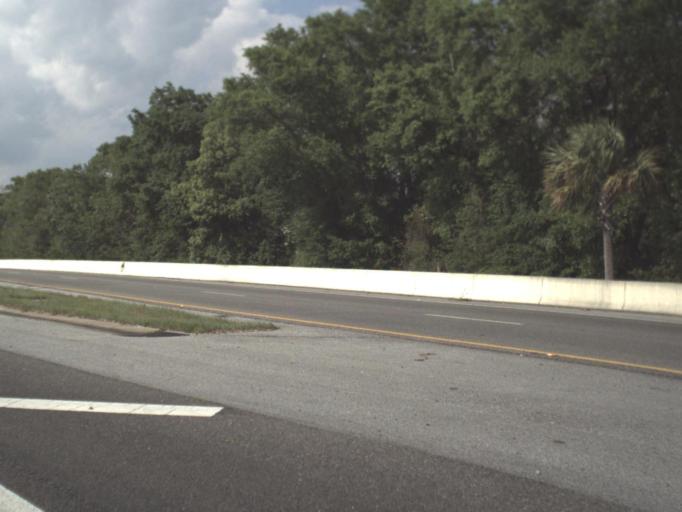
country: US
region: Florida
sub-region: Escambia County
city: Brent
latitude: 30.4690
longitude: -87.2273
